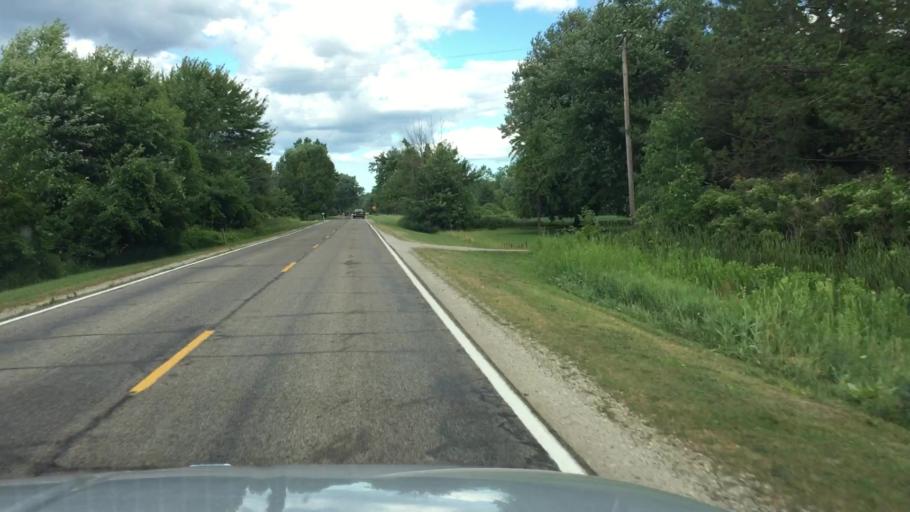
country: US
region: Michigan
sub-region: Saint Clair County
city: Yale
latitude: 43.1281
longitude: -82.8825
